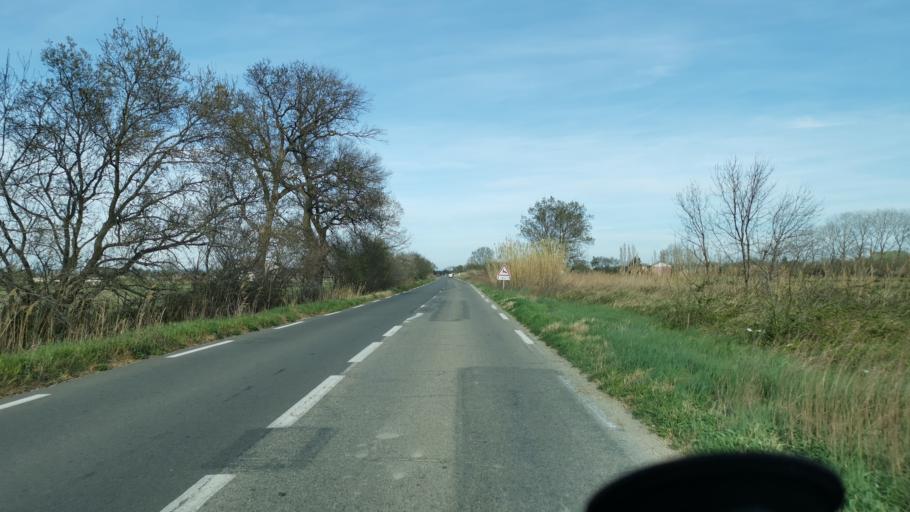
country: FR
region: Provence-Alpes-Cote d'Azur
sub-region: Departement des Bouches-du-Rhone
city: Saint-Martin-de-Crau
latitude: 43.5611
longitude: 4.7334
